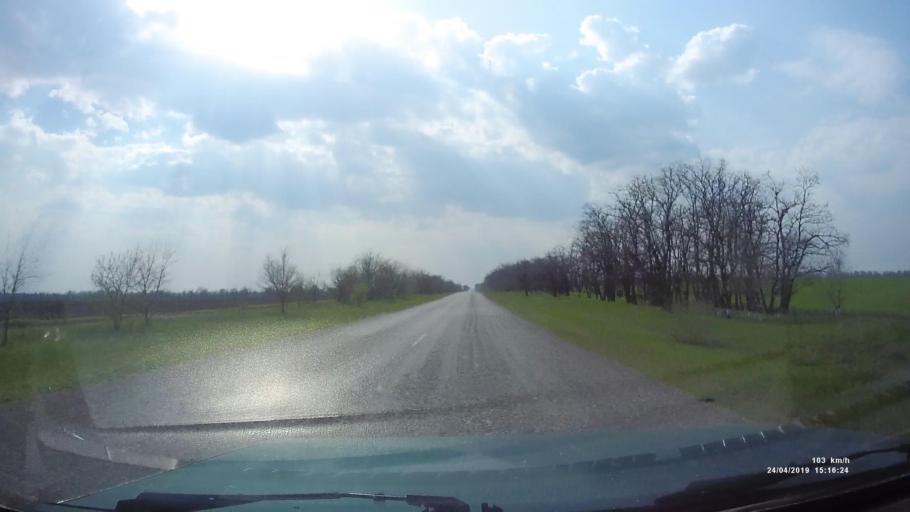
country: RU
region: Rostov
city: Remontnoye
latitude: 46.5465
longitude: 43.2137
